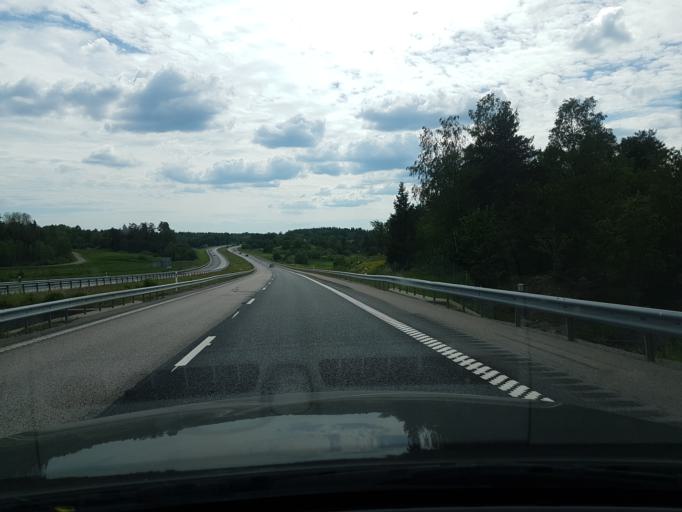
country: SE
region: Stockholm
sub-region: Norrtalje Kommun
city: Norrtalje
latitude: 59.7265
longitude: 18.5577
